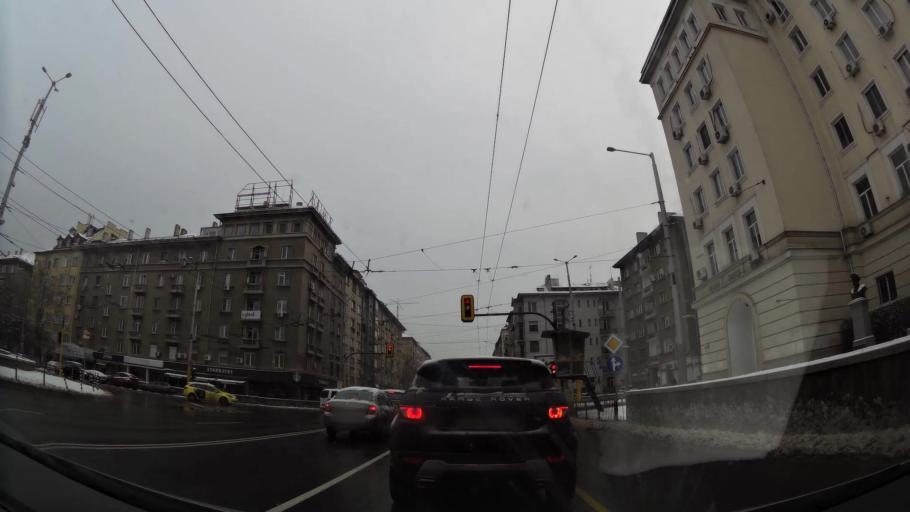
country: BG
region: Sofia-Capital
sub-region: Stolichna Obshtina
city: Sofia
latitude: 42.6903
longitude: 23.3316
